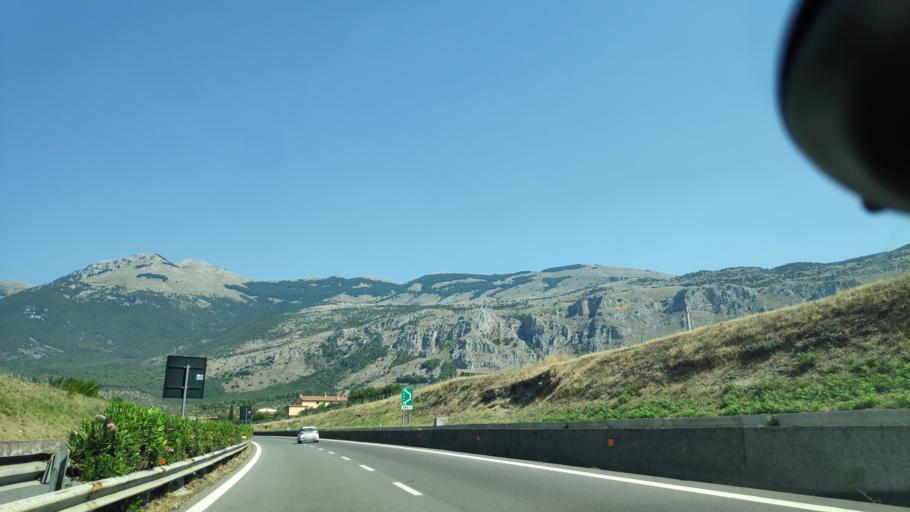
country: IT
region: Calabria
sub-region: Provincia di Cosenza
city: Frascineto
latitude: 39.8267
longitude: 16.2597
